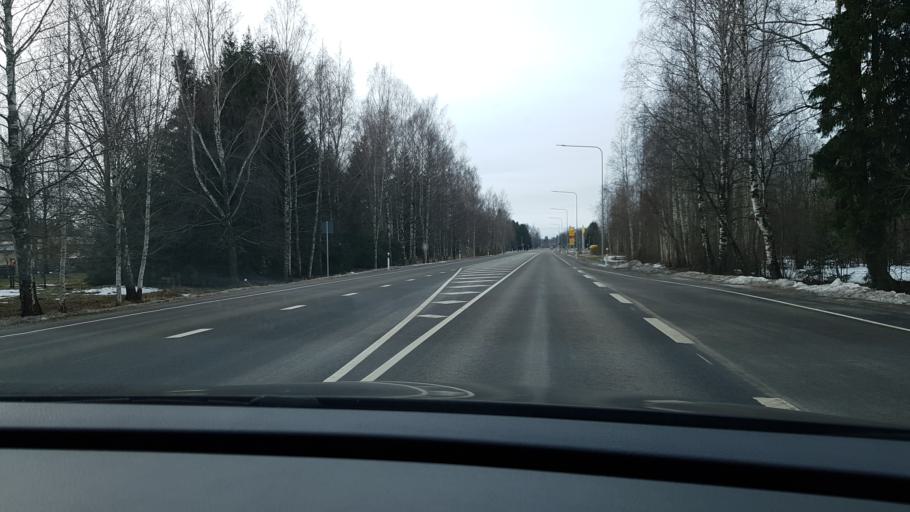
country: EE
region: Paernumaa
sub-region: Sindi linn
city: Sindi
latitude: 58.4060
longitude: 24.6647
